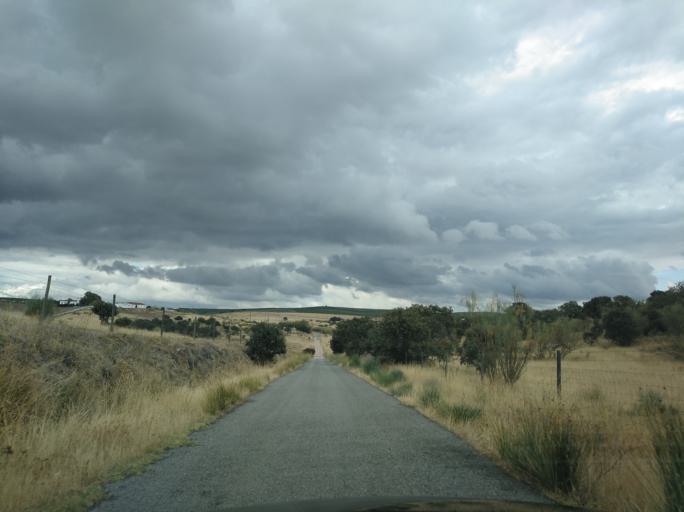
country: PT
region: Portalegre
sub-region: Campo Maior
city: Campo Maior
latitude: 39.0365
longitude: -7.1387
